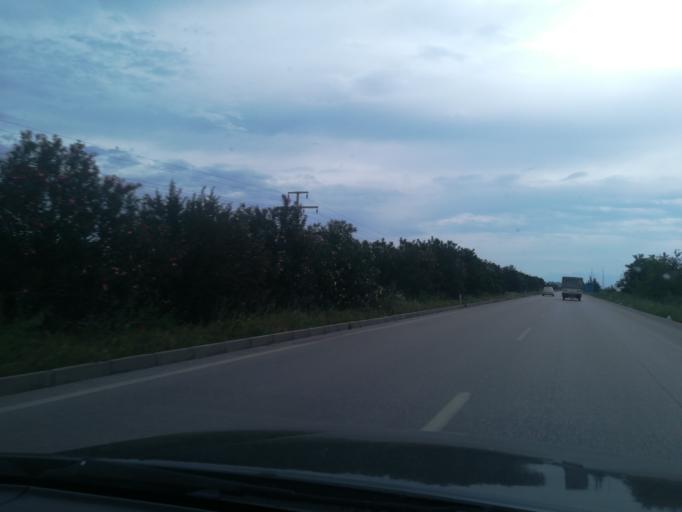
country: TR
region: Adana
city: Kosreli
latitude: 37.0619
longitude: 35.9335
